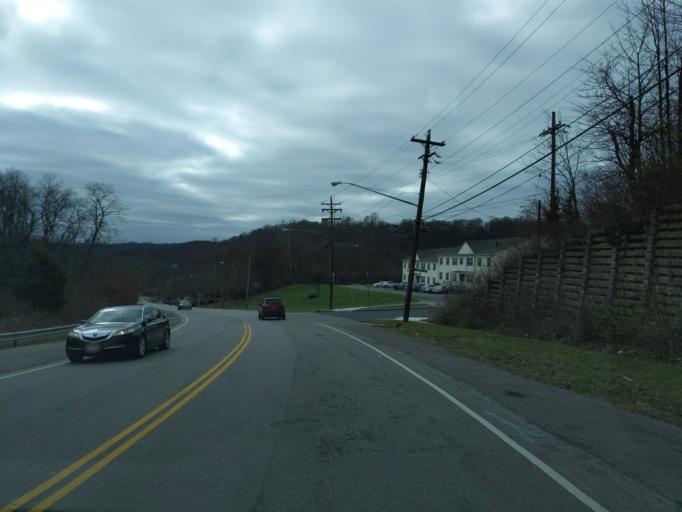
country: US
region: Ohio
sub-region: Hamilton County
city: Finneytown
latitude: 39.1783
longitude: -84.5456
